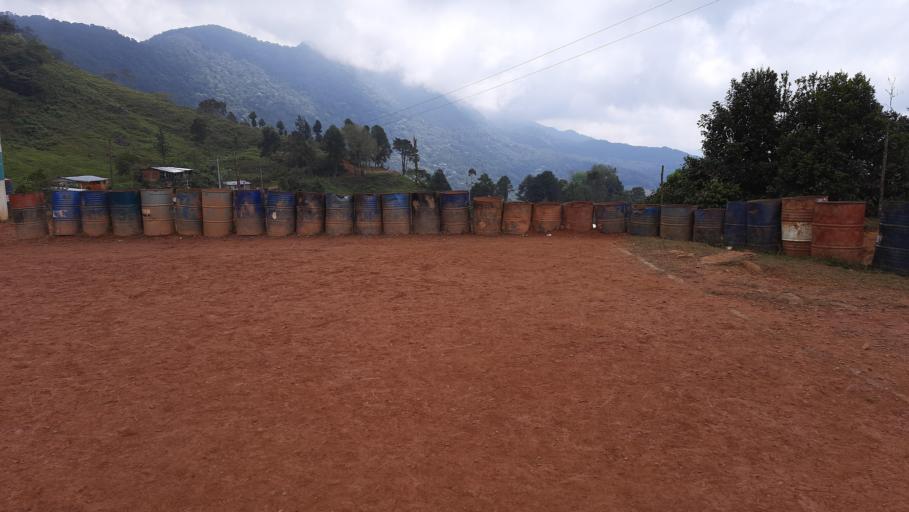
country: CO
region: Cauca
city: Buenos Aires
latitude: 3.1779
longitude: -76.7236
